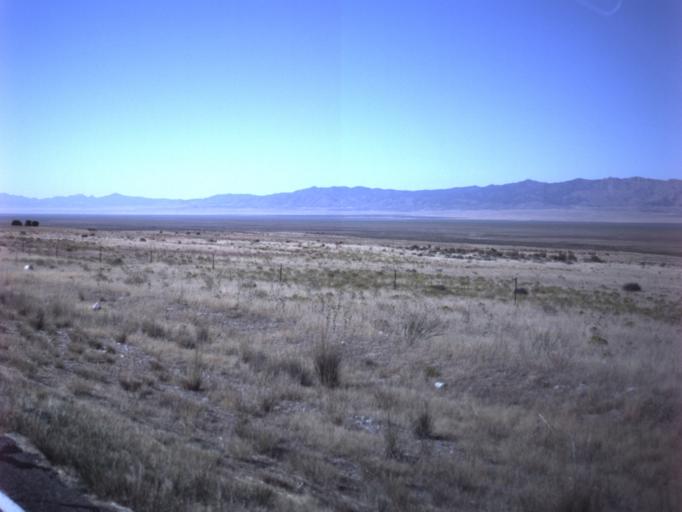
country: US
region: Utah
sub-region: Tooele County
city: Grantsville
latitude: 40.5887
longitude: -112.7216
